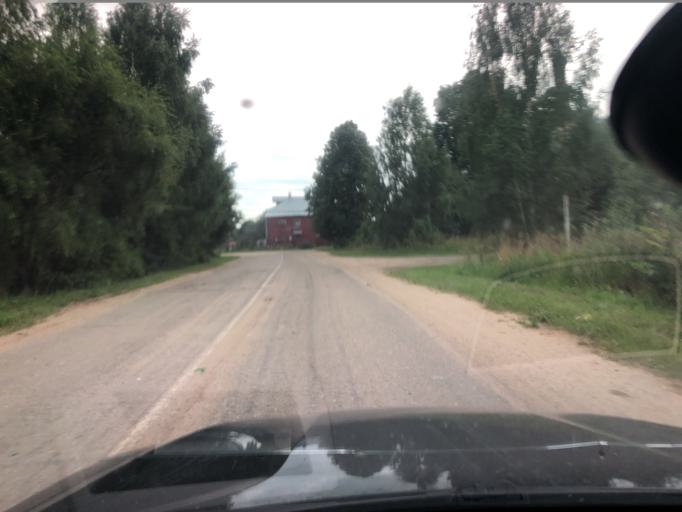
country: RU
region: Jaroslavl
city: Pereslavl'-Zalesskiy
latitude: 57.0297
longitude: 38.9142
